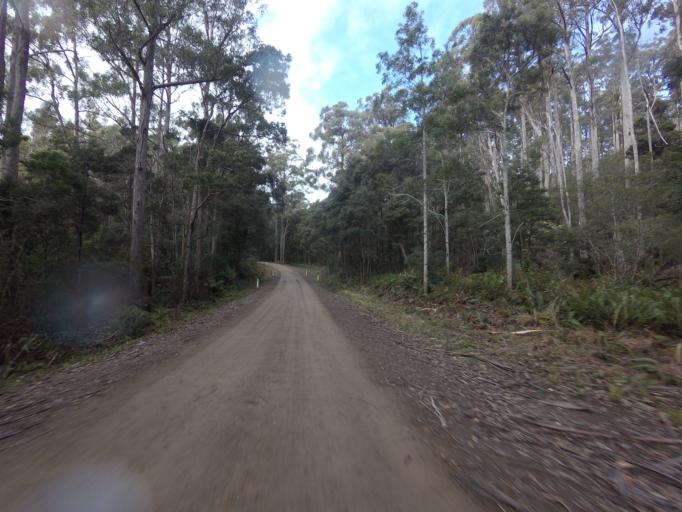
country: AU
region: Tasmania
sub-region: Huon Valley
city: Geeveston
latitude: -43.5685
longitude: 146.8893
